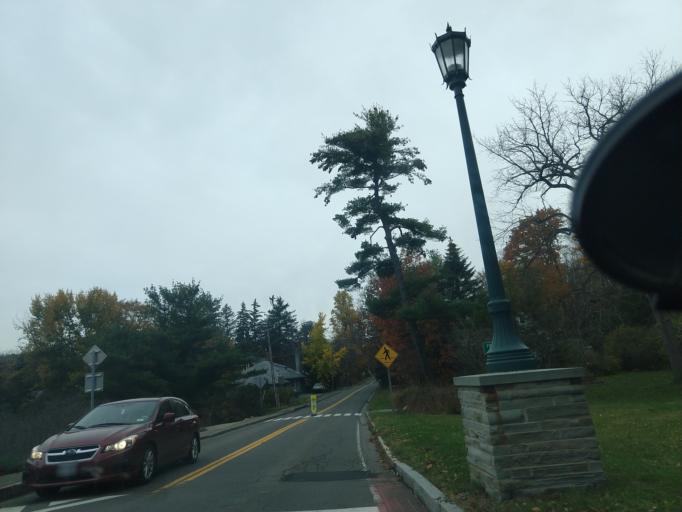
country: US
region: New York
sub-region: Tompkins County
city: East Ithaca
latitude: 42.4496
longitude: -76.4709
